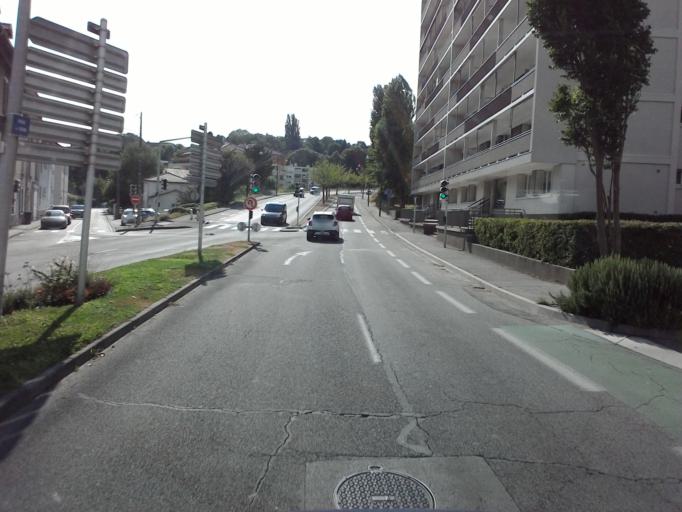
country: FR
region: Rhone-Alpes
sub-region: Departement de l'Isere
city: Voiron
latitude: 45.3694
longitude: 5.5842
